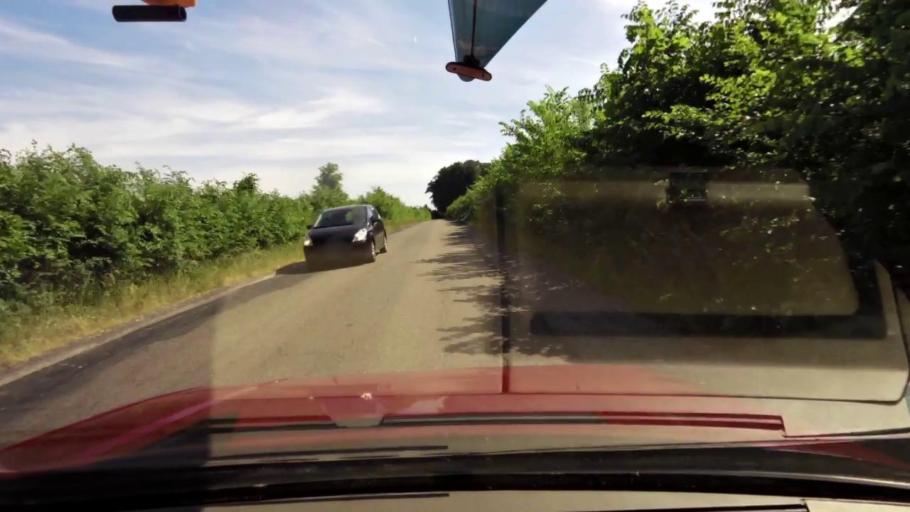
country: PL
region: Pomeranian Voivodeship
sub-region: Powiat slupski
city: Kobylnica
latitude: 54.3719
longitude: 16.9665
